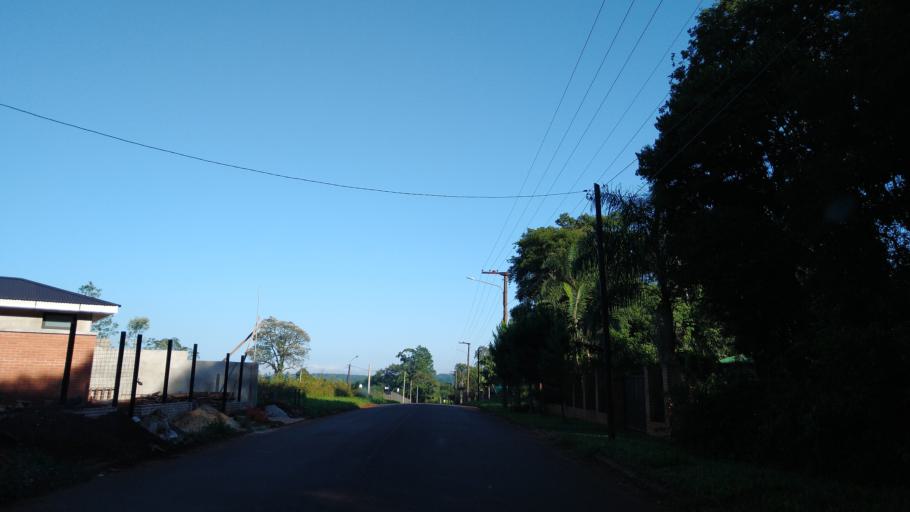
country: AR
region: Misiones
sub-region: Departamento de Montecarlo
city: Montecarlo
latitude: -26.5665
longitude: -54.7494
